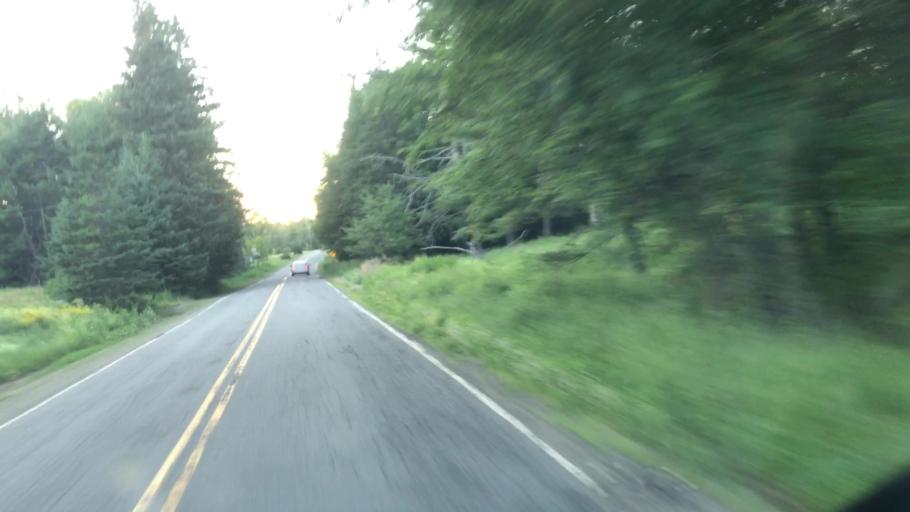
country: US
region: Maine
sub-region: Penobscot County
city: Medway
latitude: 45.6097
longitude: -68.2575
